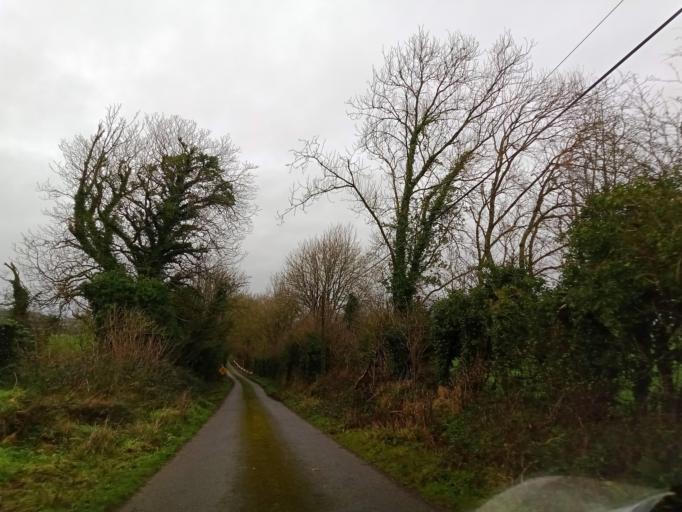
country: IE
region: Munster
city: Fethard
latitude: 52.5586
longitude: -7.7072
